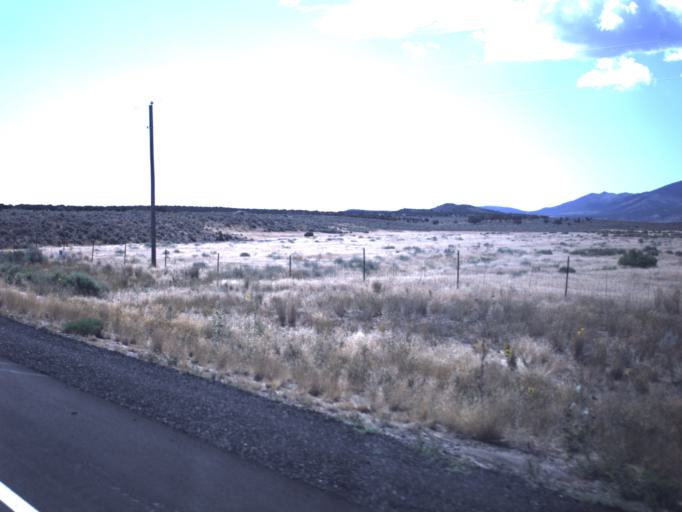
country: US
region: Utah
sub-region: Utah County
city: Eagle Mountain
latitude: 40.0724
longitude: -112.3352
